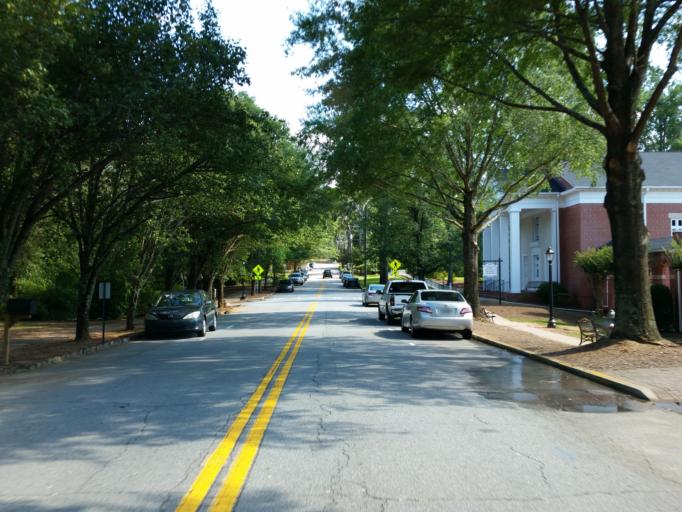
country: US
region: Georgia
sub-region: Fulton County
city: Roswell
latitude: 34.0180
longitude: -84.3635
